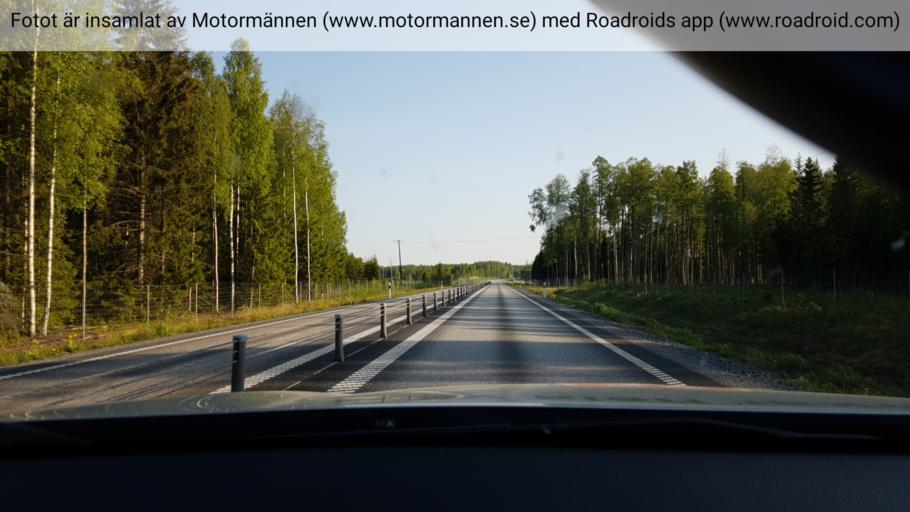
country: SE
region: Uppsala
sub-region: Heby Kommun
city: Heby
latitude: 60.0390
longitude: 16.8721
